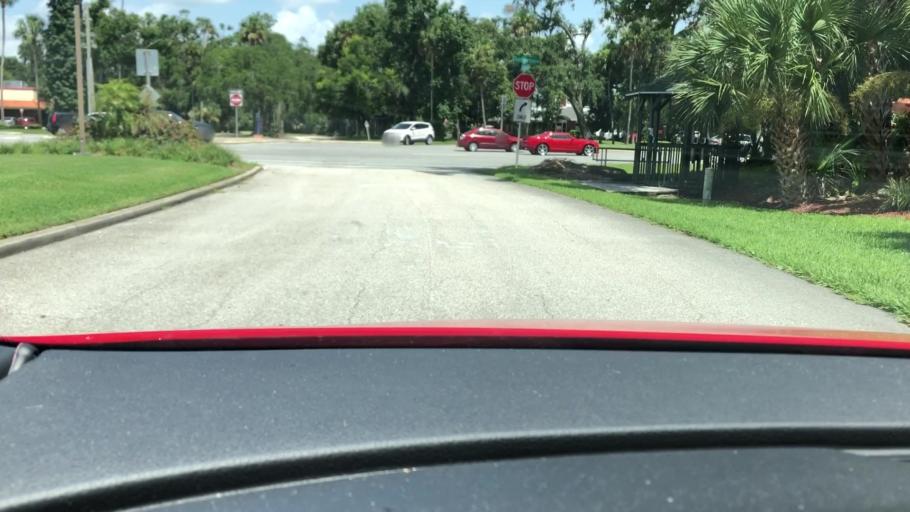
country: US
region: Florida
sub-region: Volusia County
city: Port Orange
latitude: 29.1259
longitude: -81.0068
